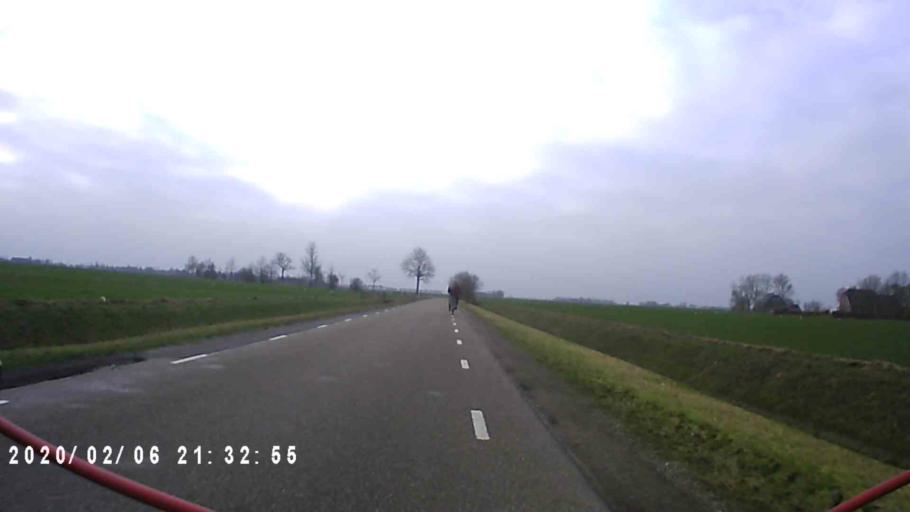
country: NL
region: Groningen
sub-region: Gemeente Zuidhorn
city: Noordhorn
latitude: 53.2784
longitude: 6.3906
